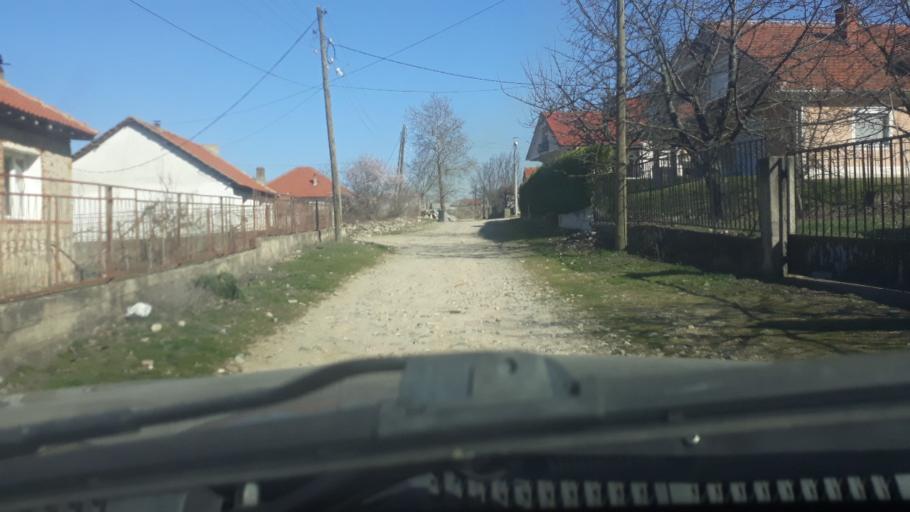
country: MK
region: Novo Selo
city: Susica
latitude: 41.3803
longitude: 22.8178
